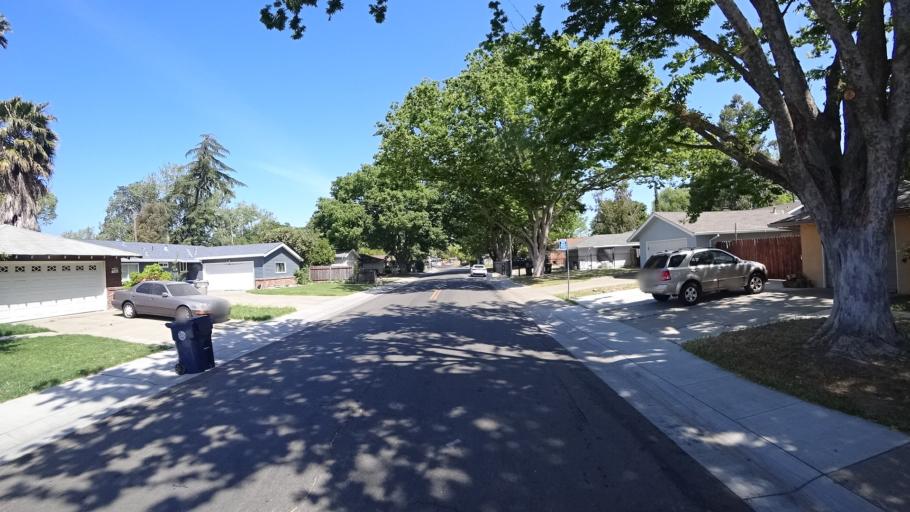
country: US
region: California
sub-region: Sacramento County
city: Parkway
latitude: 38.4974
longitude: -121.4913
